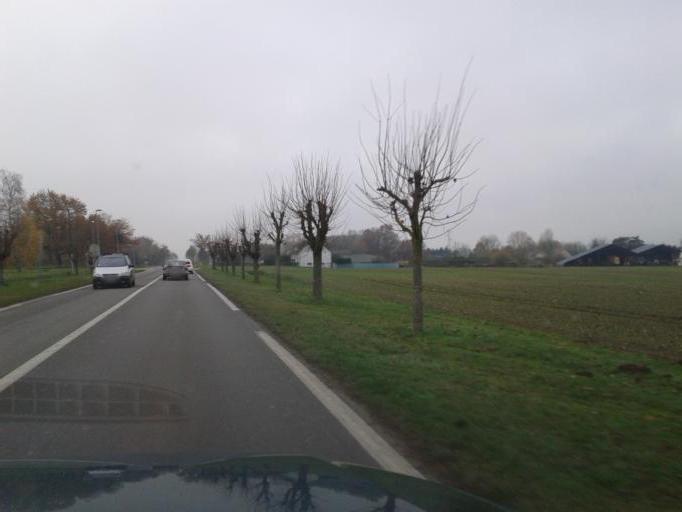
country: FR
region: Centre
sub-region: Departement du Loiret
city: Clery-Saint-Andre
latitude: 47.8118
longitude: 1.7449
